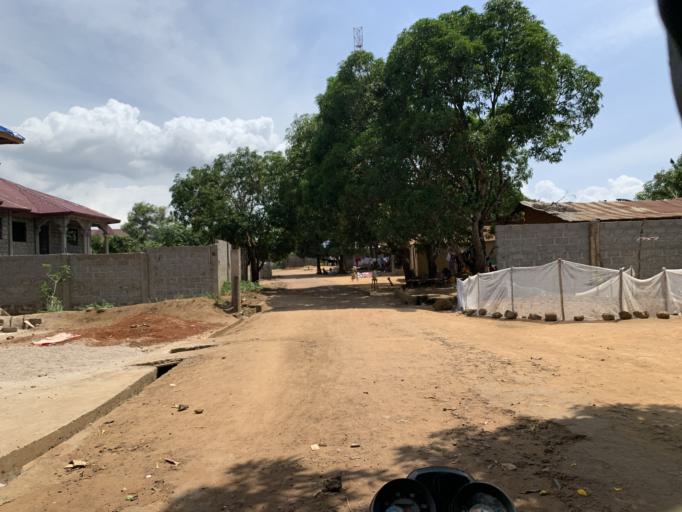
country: SL
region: Western Area
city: Waterloo
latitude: 8.3364
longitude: -13.0373
